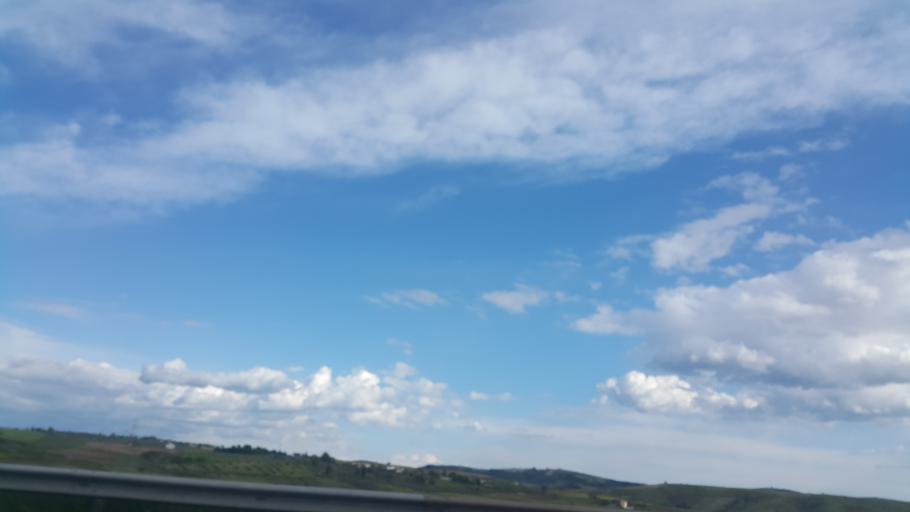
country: TR
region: Adana
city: Ceyhan
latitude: 36.9870
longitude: 35.9007
